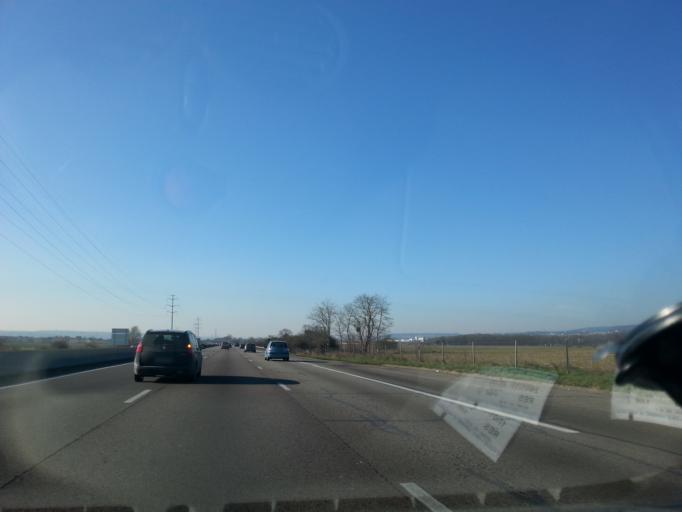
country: FR
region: Ile-de-France
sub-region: Departement des Yvelines
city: Bouafle
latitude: 48.9706
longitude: 1.8914
